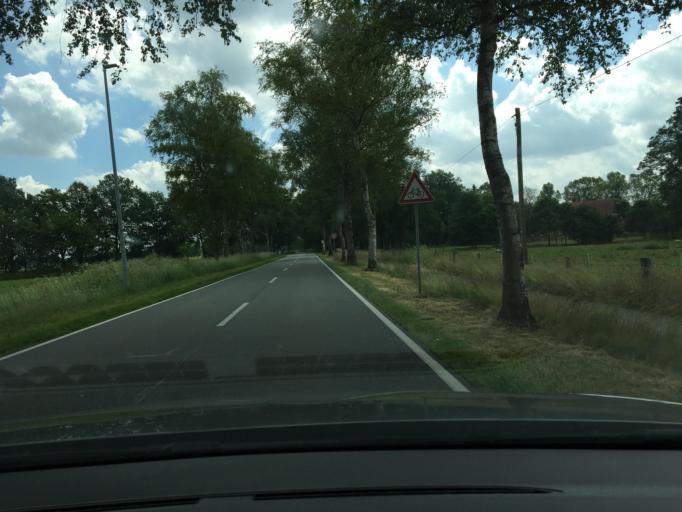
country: DE
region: Lower Saxony
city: Tarmstedt
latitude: 53.2426
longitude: 9.0243
